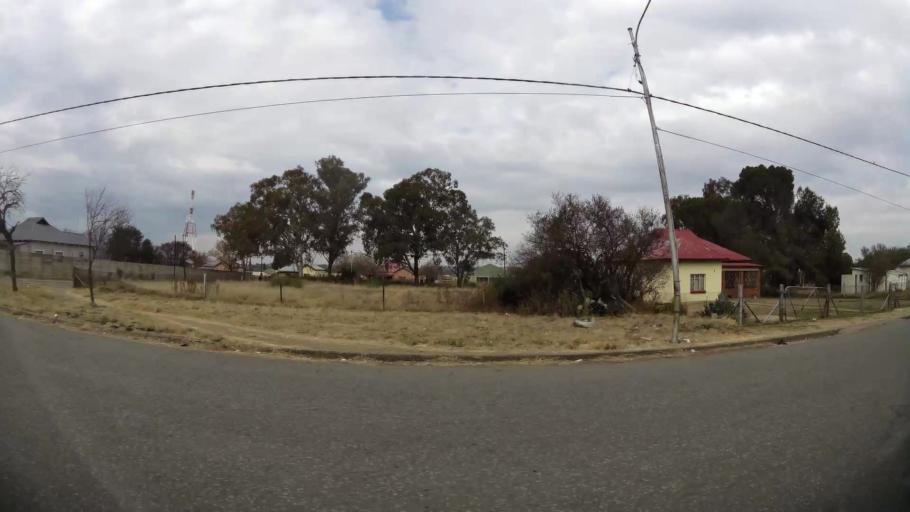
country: ZA
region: Orange Free State
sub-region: Fezile Dabi District Municipality
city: Kroonstad
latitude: -27.6570
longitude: 27.2316
